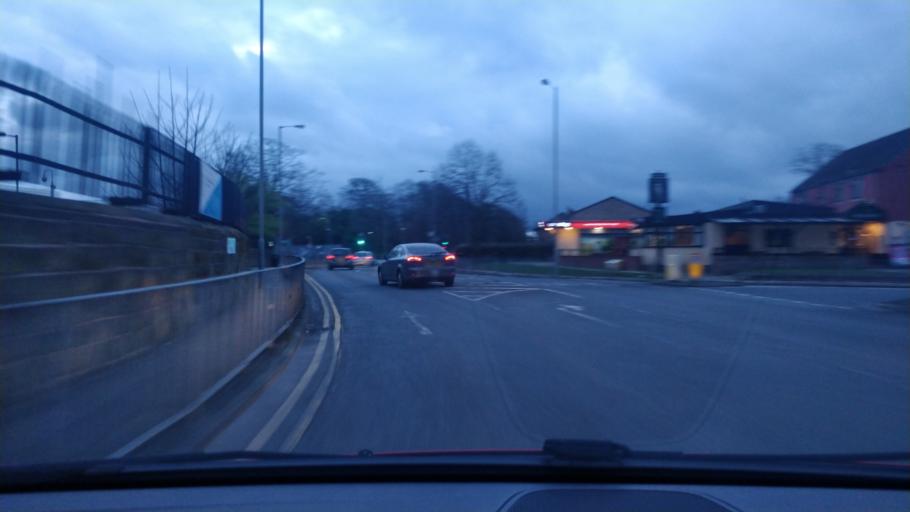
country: GB
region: England
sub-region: Knowsley
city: Knowsley
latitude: 53.4249
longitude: -2.8897
